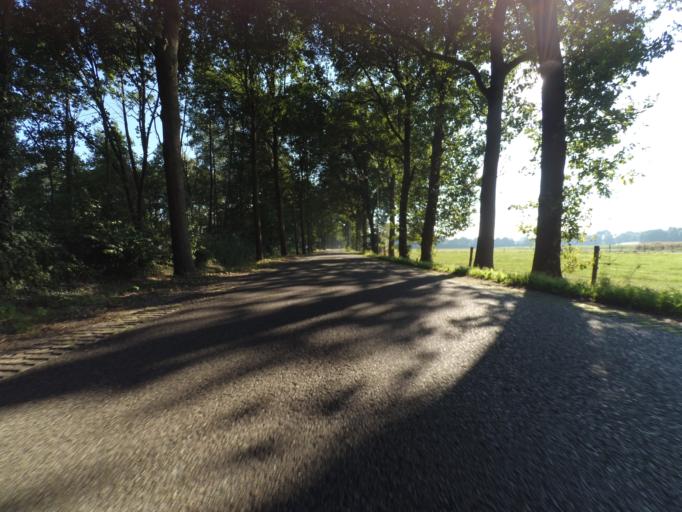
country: NL
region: Gelderland
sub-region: Gemeente Putten
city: Putten
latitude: 52.2478
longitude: 5.5911
